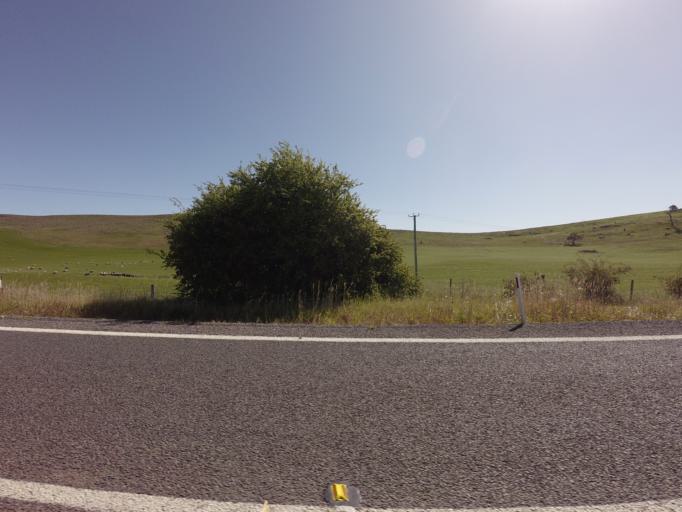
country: AU
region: Tasmania
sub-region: Derwent Valley
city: New Norfolk
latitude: -42.5776
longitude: 146.8818
